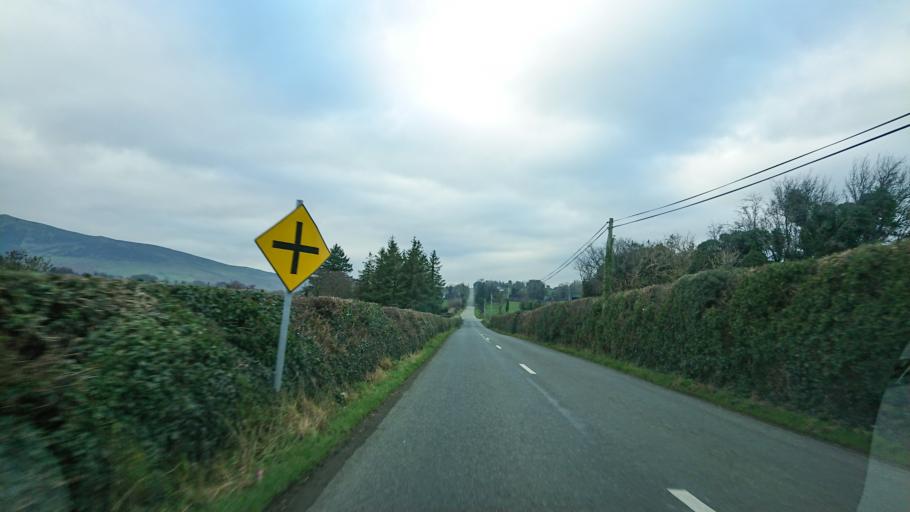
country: IE
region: Munster
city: Carrick-on-Suir
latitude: 52.3178
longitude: -7.5493
